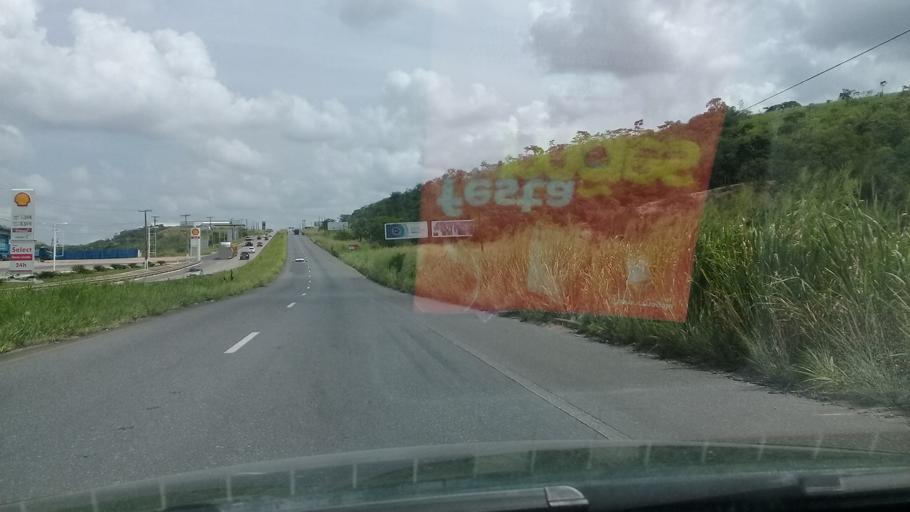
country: BR
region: Pernambuco
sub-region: Vitoria De Santo Antao
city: Vitoria de Santo Antao
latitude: -8.1144
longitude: -35.2477
